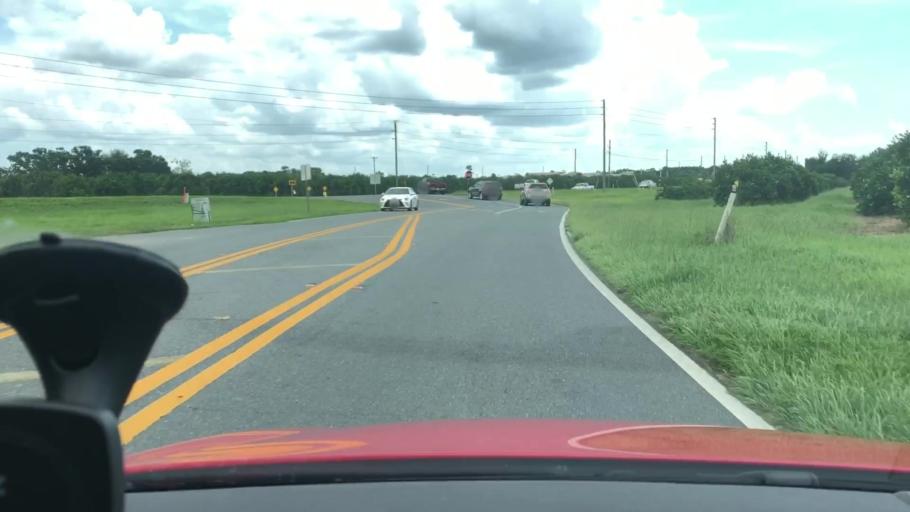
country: US
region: Florida
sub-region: Lake County
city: Mount Dora
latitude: 28.8313
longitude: -81.6440
